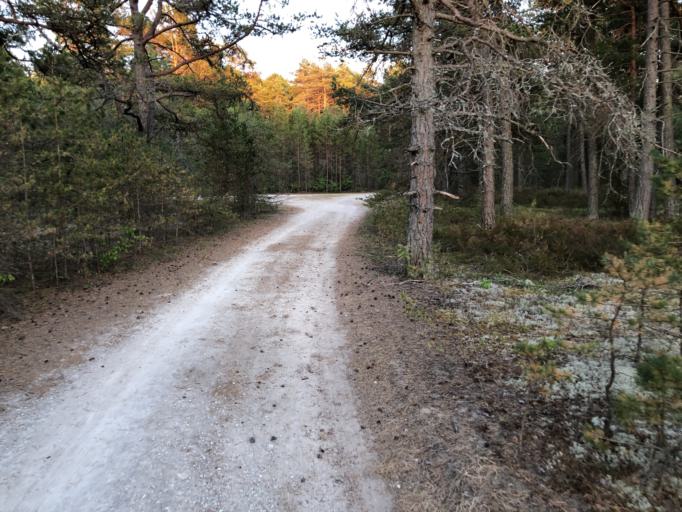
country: EE
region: Harju
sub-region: Paldiski linn
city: Paldiski
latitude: 59.3902
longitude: 24.2319
